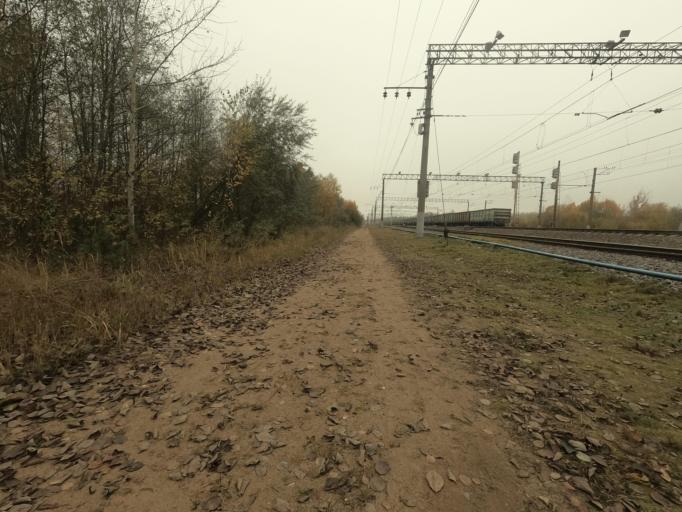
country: RU
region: Leningrad
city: Pavlovo
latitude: 59.7664
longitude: 30.9561
